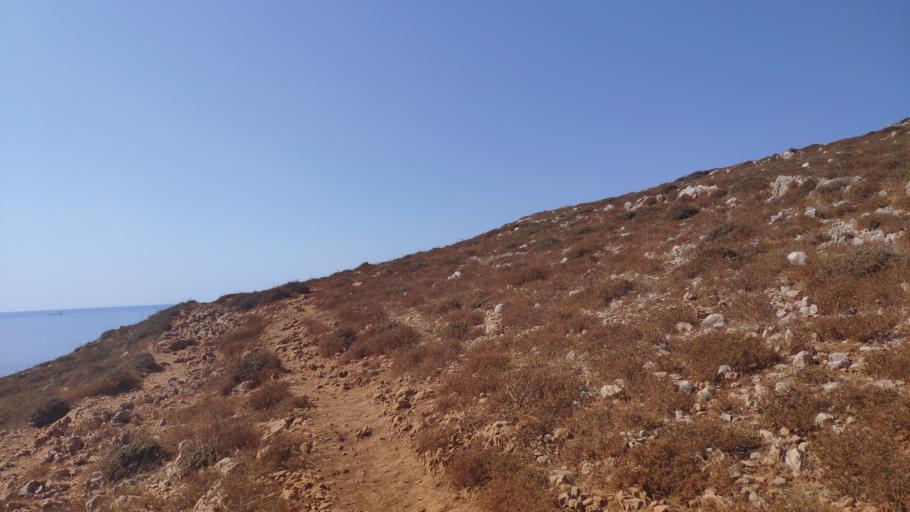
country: GR
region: Peloponnese
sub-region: Nomos Lakonias
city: Gytheio
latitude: 36.3924
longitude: 22.4837
